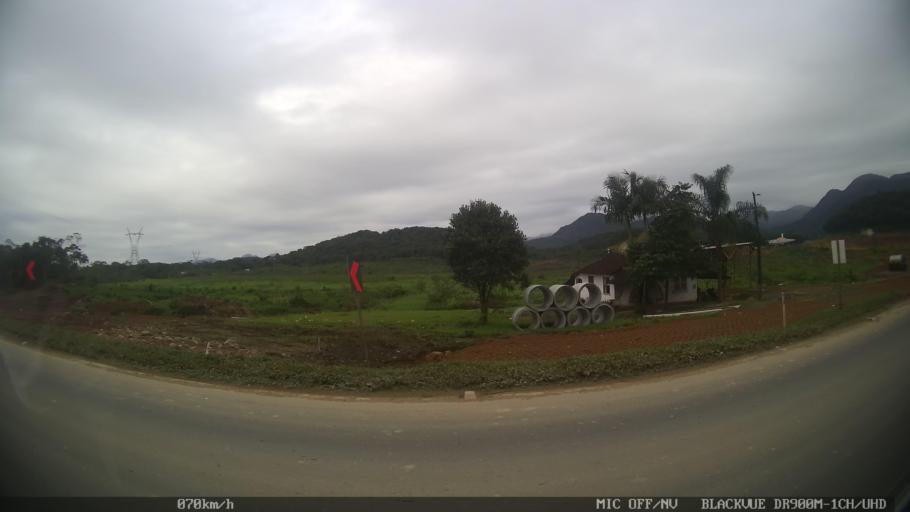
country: BR
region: Santa Catarina
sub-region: Joinville
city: Joinville
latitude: -26.2538
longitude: -48.9062
